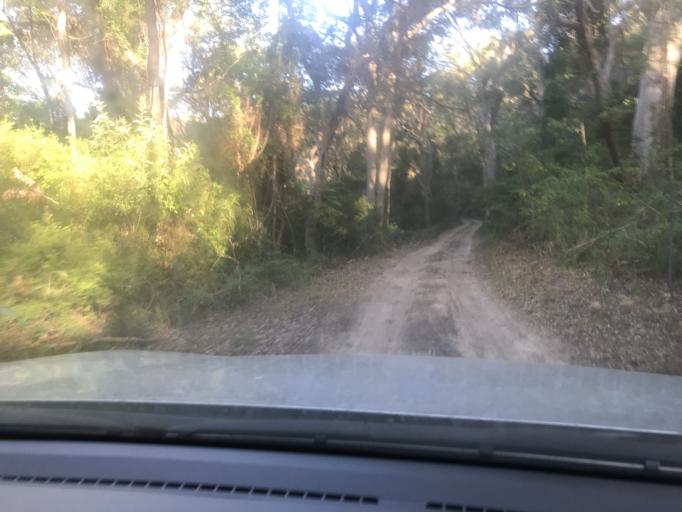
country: AU
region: Queensland
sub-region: Fraser Coast
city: Urangan
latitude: -25.3794
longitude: 153.1668
